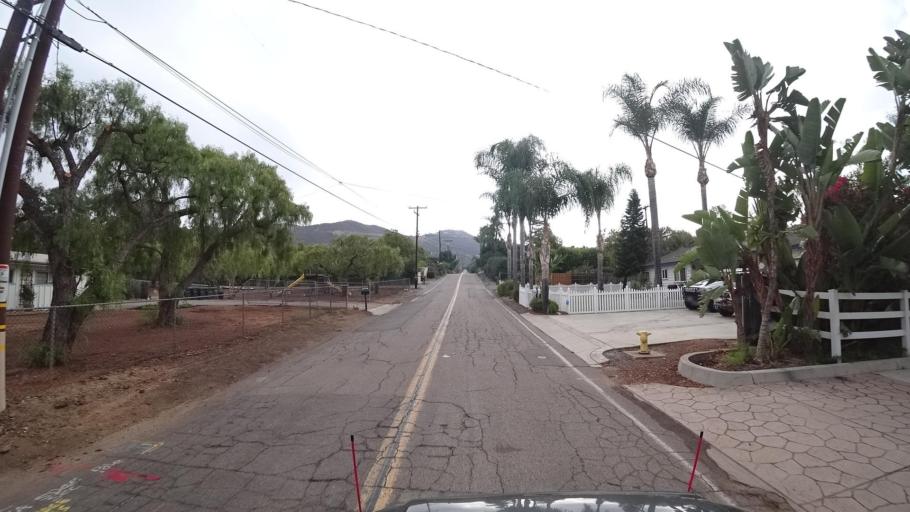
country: US
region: California
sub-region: San Diego County
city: Vista
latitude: 33.2084
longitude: -117.2035
